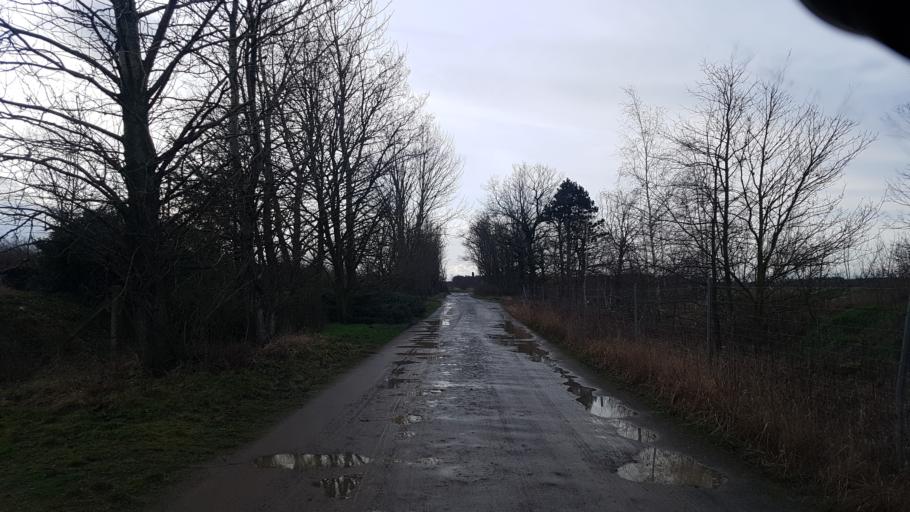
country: DE
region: Brandenburg
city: Herzberg
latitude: 51.6772
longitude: 13.2390
